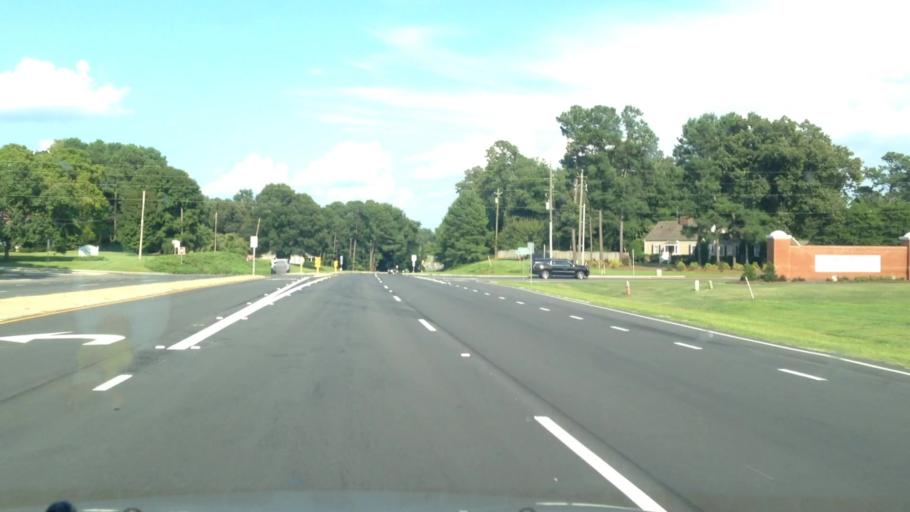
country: US
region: North Carolina
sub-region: Harnett County
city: Buies Creek
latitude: 35.4074
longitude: -78.7532
